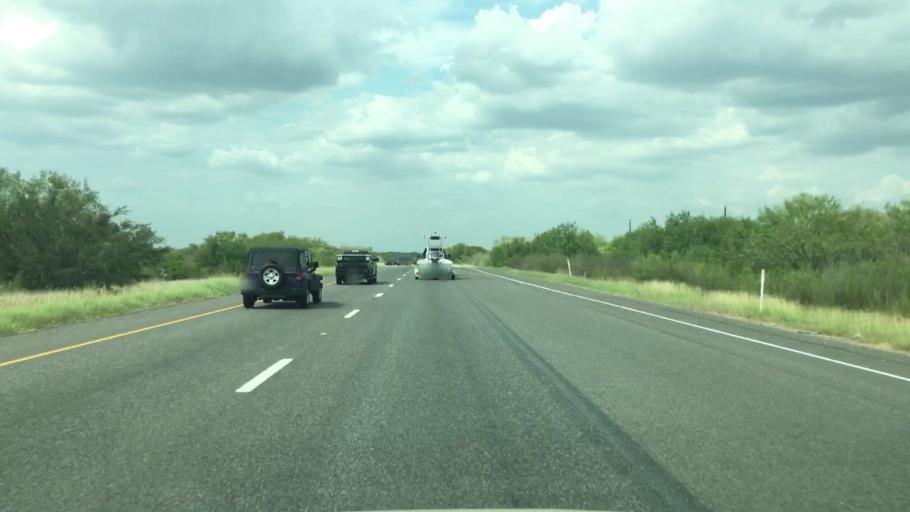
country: US
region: Texas
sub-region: Atascosa County
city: Pleasanton
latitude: 28.9204
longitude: -98.4347
